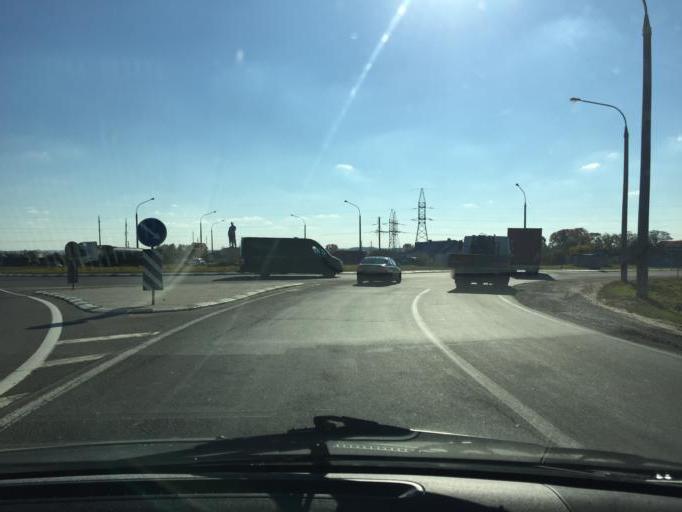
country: BY
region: Minsk
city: Salihorsk
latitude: 52.8538
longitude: 27.4667
